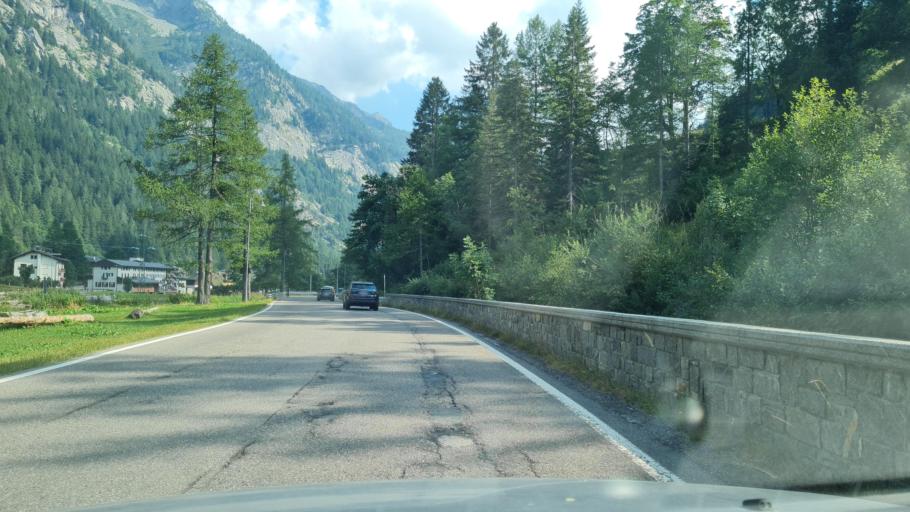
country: IT
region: Piedmont
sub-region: Provincia Verbano-Cusio-Ossola
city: Formazza
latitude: 46.3703
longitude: 8.4277
